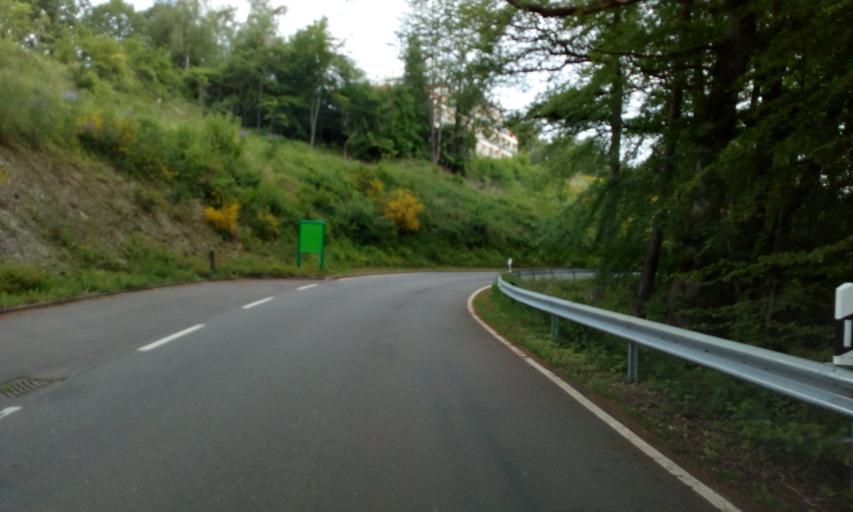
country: DE
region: Rheinland-Pfalz
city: Leiwen
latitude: 49.8046
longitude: 6.8926
